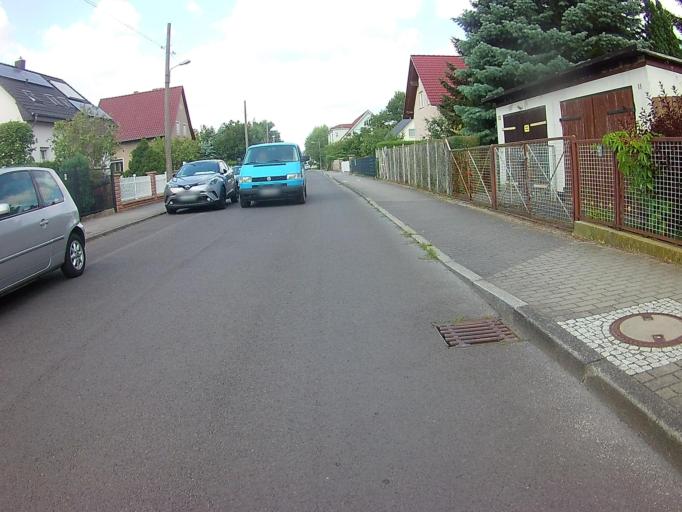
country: DE
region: Berlin
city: Bohnsdorf
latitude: 52.3964
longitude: 13.5639
